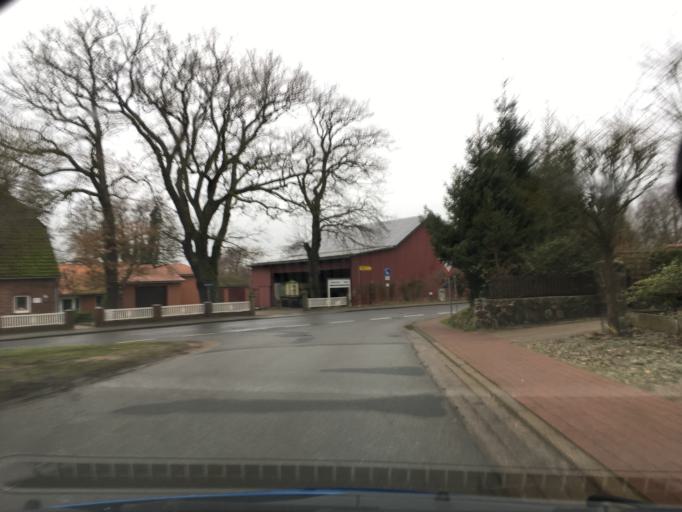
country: DE
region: Lower Saxony
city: Neetze
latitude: 53.2682
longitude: 10.6256
